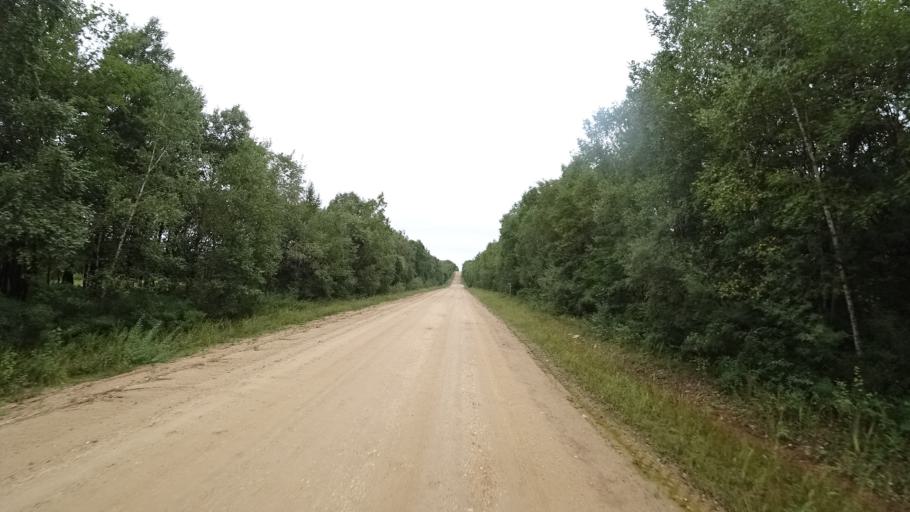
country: RU
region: Primorskiy
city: Ivanovka
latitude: 44.0400
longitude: 132.5386
